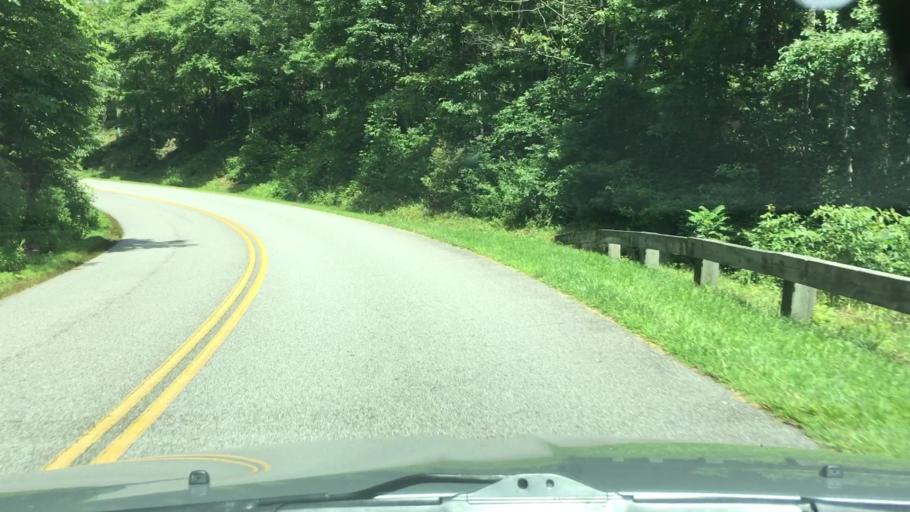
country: US
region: North Carolina
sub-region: Buncombe County
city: Weaverville
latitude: 35.6557
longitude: -82.4840
